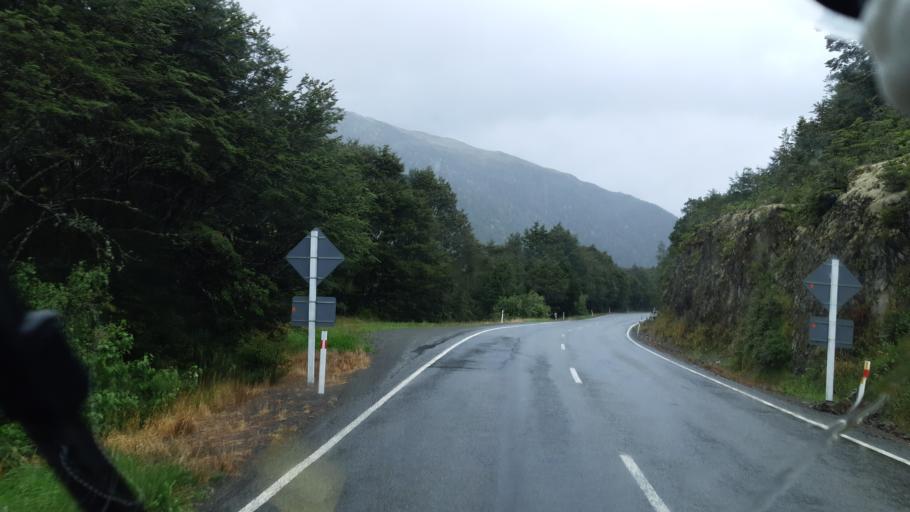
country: NZ
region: Canterbury
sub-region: Hurunui District
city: Amberley
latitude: -42.3986
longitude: 172.3988
